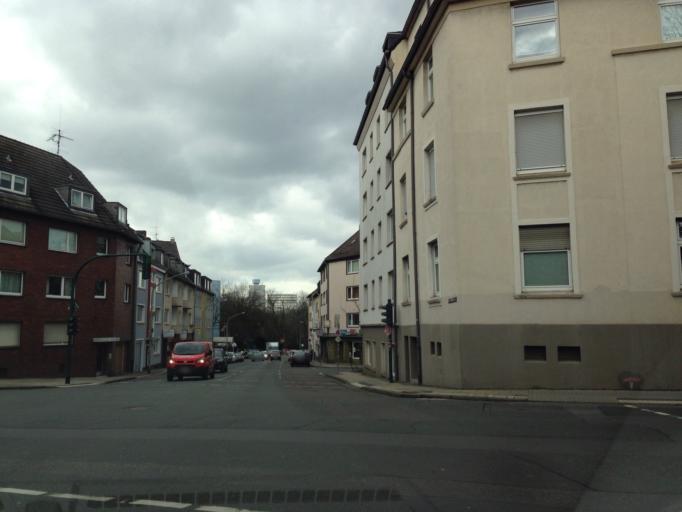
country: DE
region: North Rhine-Westphalia
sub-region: Regierungsbezirk Dusseldorf
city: Essen
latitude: 51.4411
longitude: 7.0122
